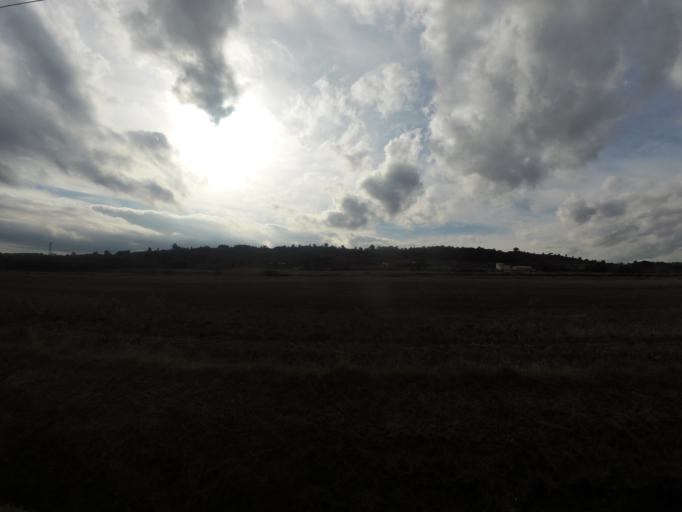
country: FR
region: Languedoc-Roussillon
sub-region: Departement du Gard
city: Saint-Mamert-du-Gard
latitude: 43.8953
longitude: 4.2260
